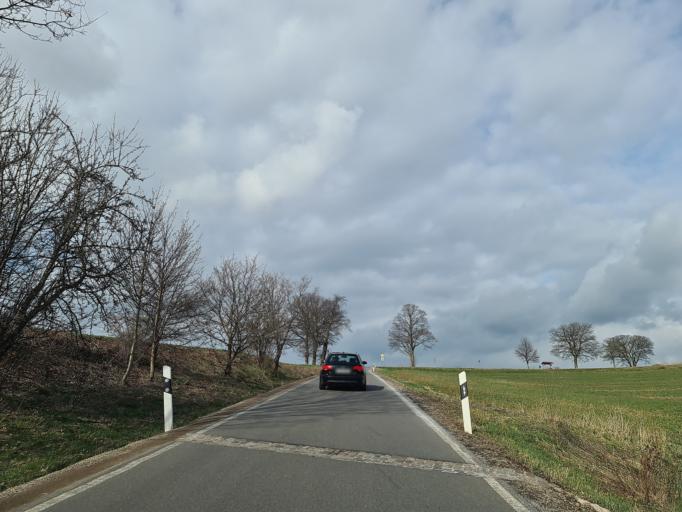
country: DE
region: Saxony
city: Lichtenstein
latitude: 50.7174
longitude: 12.6223
